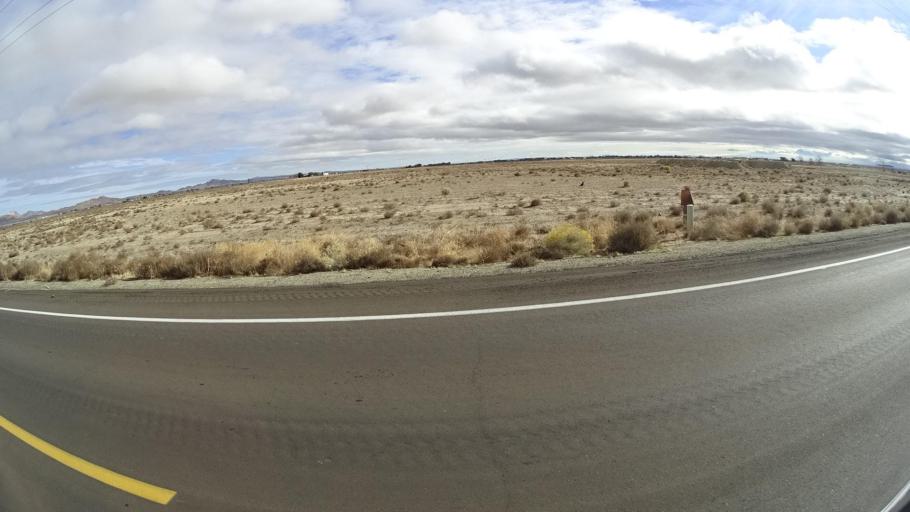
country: US
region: California
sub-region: Kern County
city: Rosamond
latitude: 34.8283
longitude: -118.2906
